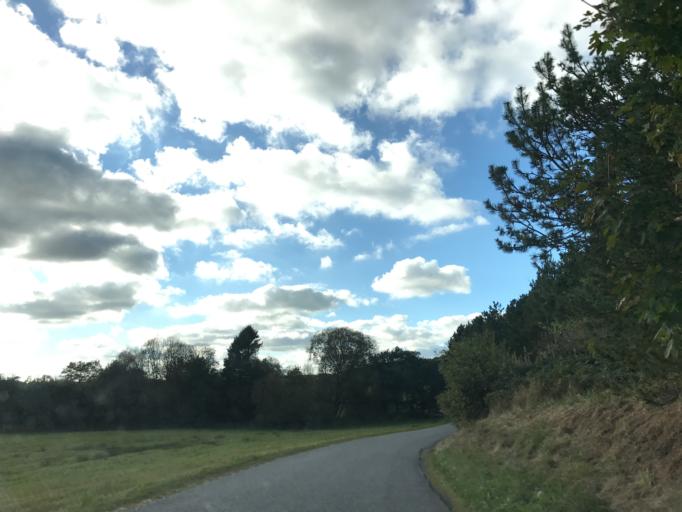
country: DK
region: Central Jutland
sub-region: Silkeborg Kommune
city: Kjellerup
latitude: 56.2579
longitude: 9.4810
